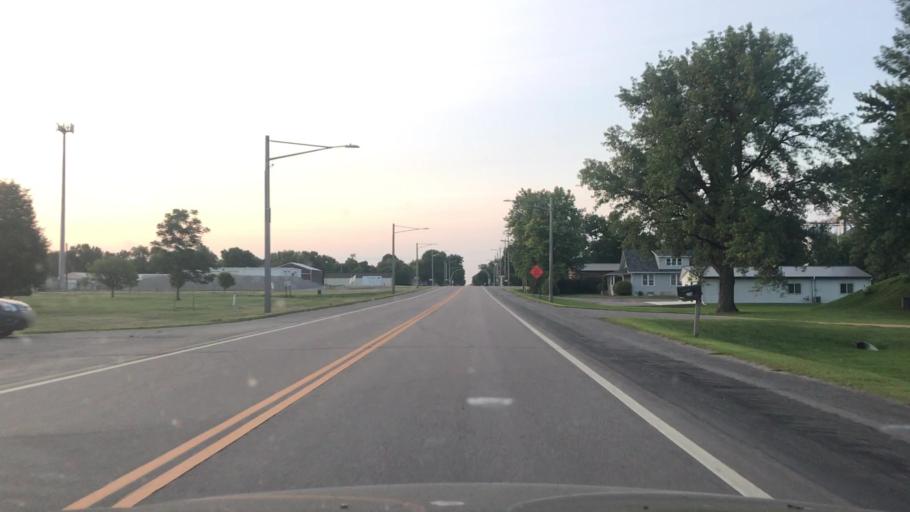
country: US
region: Minnesota
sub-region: Redwood County
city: Redwood Falls
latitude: 44.5291
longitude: -95.1195
